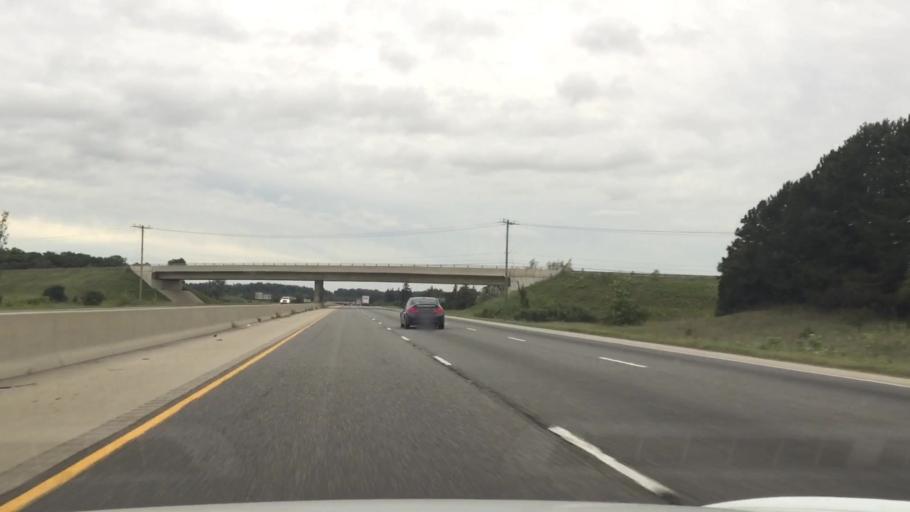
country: CA
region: Ontario
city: Kitchener
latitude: 43.3141
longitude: -80.4725
